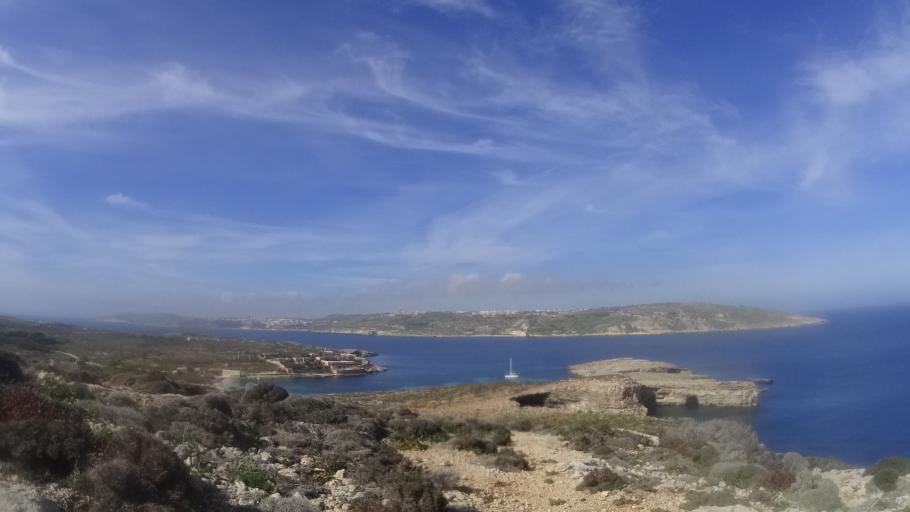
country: MT
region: Il-Qala
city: Qala
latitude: 36.0155
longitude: 14.3422
